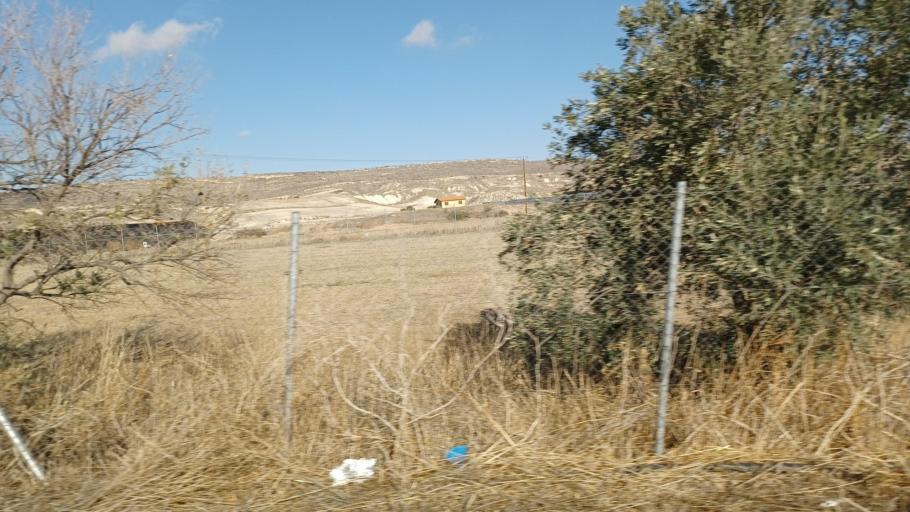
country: CY
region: Larnaka
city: Troulloi
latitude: 35.0280
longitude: 33.5999
